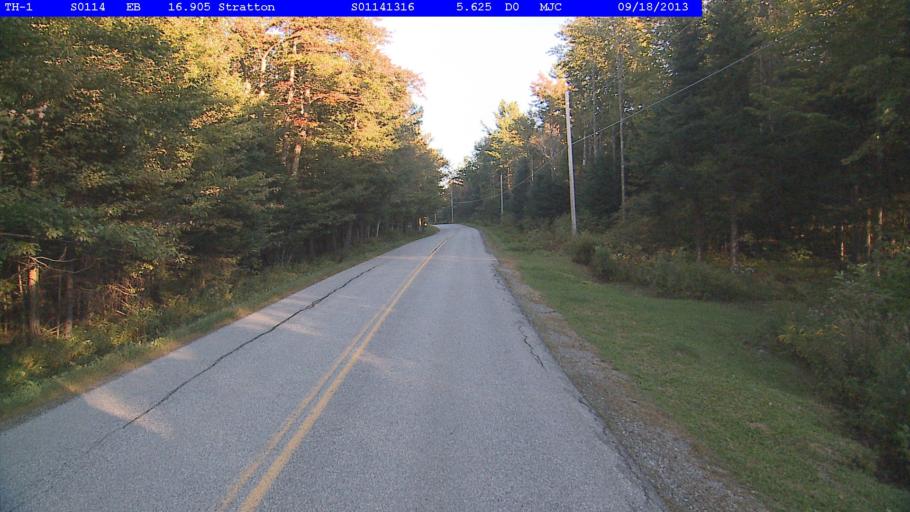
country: US
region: Vermont
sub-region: Windham County
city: Dover
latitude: 43.0396
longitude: -72.9038
